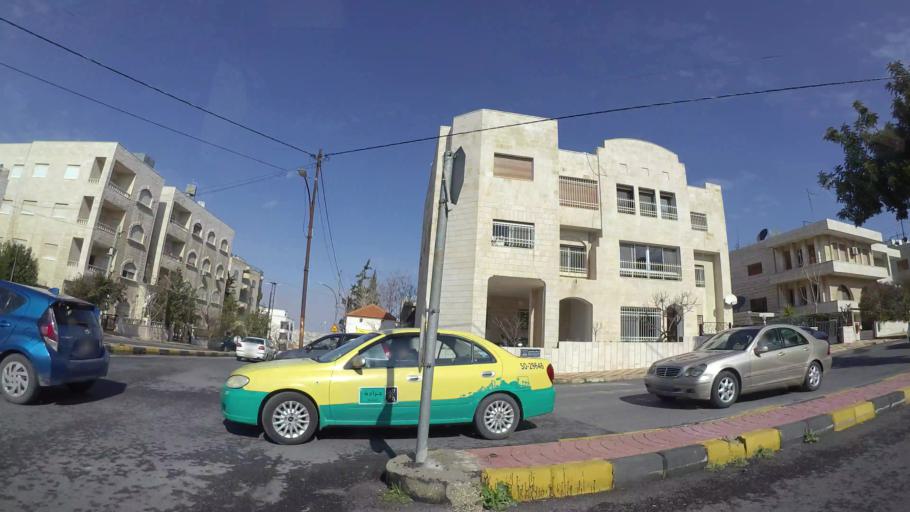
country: JO
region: Amman
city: Al Jubayhah
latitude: 32.0010
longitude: 35.8851
